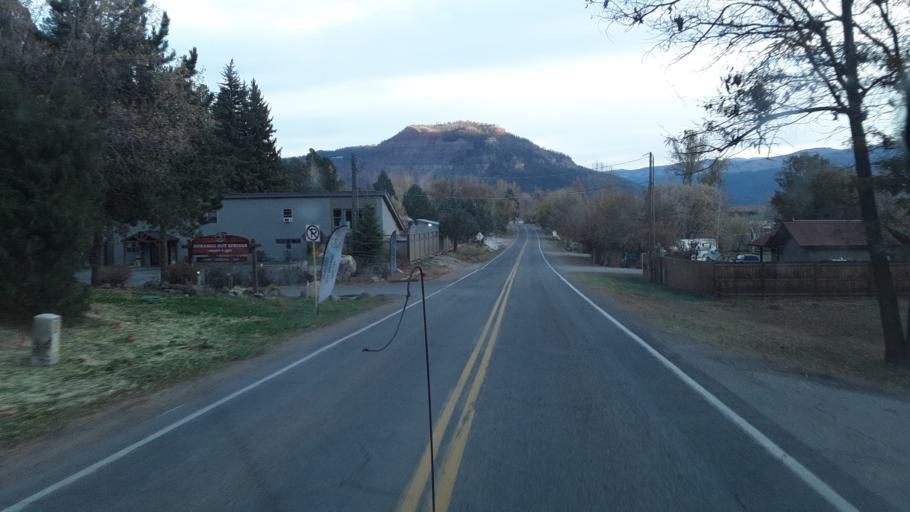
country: US
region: Colorado
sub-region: La Plata County
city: Durango
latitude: 37.3904
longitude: -107.8487
